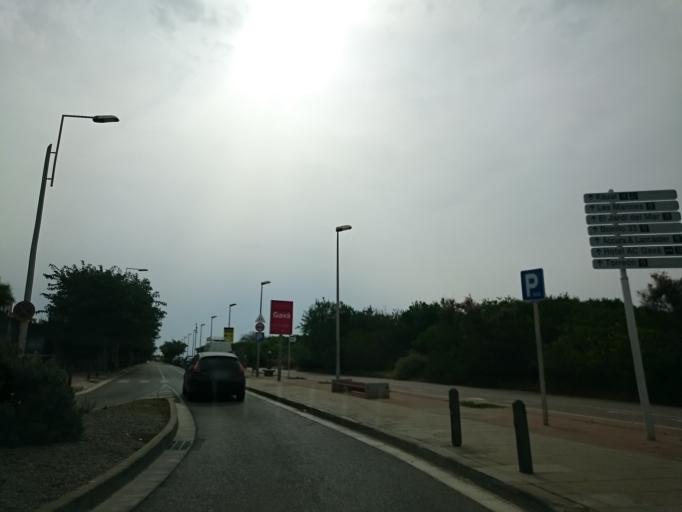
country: ES
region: Catalonia
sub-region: Provincia de Barcelona
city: Castelldefels
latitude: 41.2654
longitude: 2.0023
